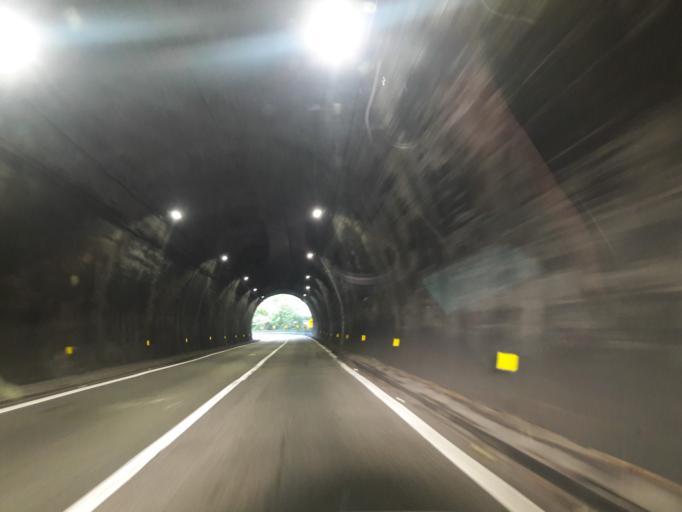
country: BR
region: Sao Paulo
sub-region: Cubatao
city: Cubatao
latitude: -23.8896
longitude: -46.4911
